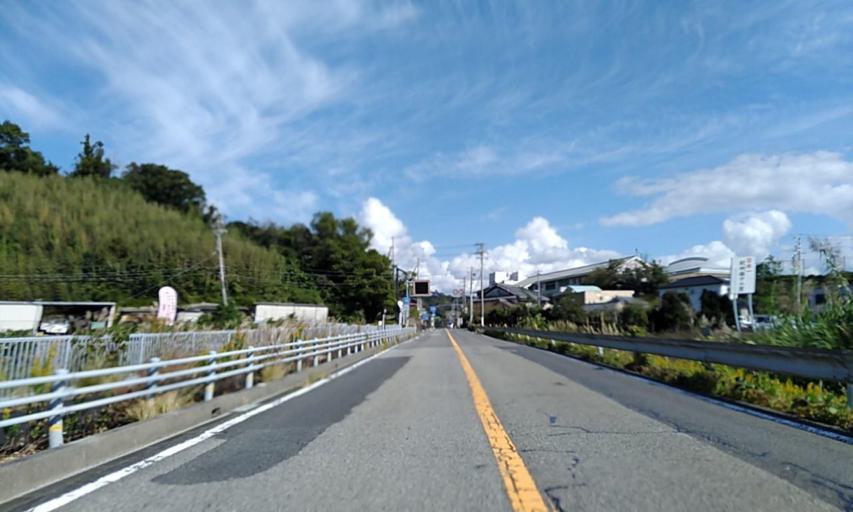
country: JP
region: Wakayama
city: Tanabe
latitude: 33.7817
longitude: 135.2787
